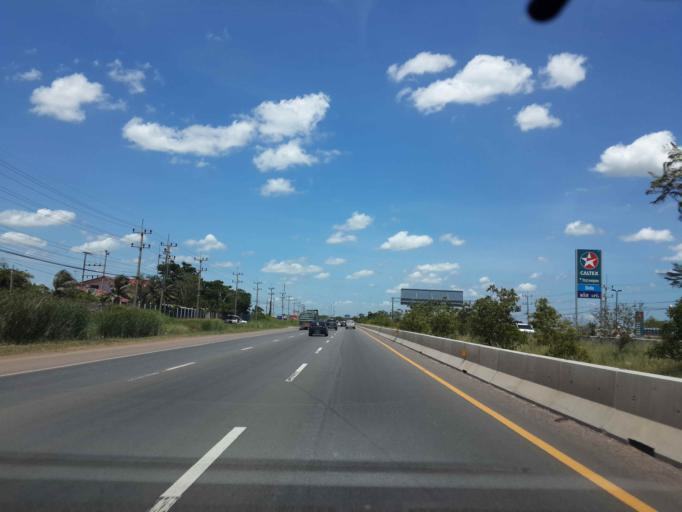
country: TH
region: Samut Songkhram
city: Samut Songkhram
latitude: 13.4432
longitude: 100.0694
